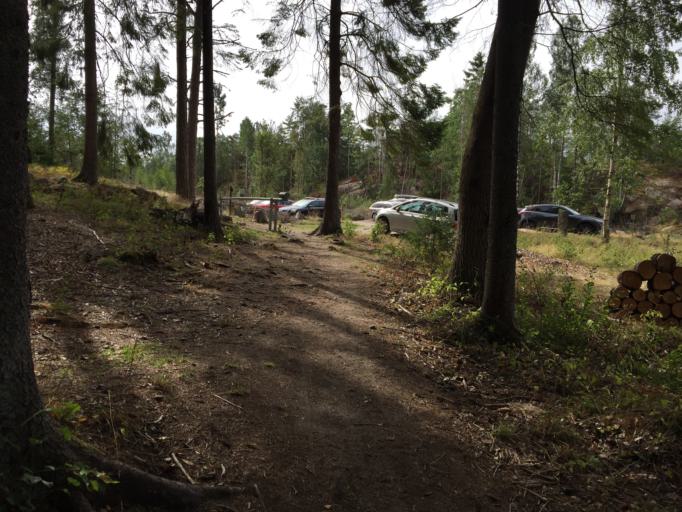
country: NO
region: Ostfold
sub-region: Fredrikstad
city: Fredrikstad
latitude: 59.0983
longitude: 10.9266
